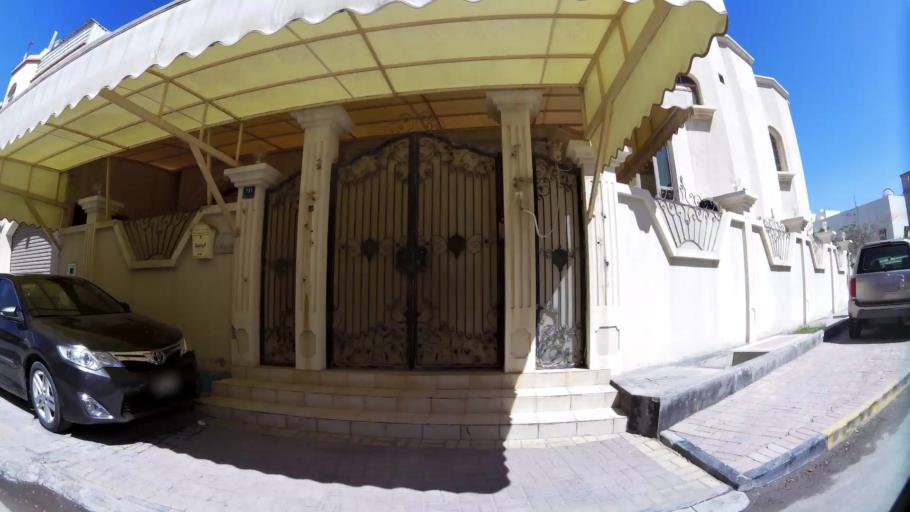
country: BH
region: Muharraq
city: Al Muharraq
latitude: 26.2791
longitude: 50.6318
